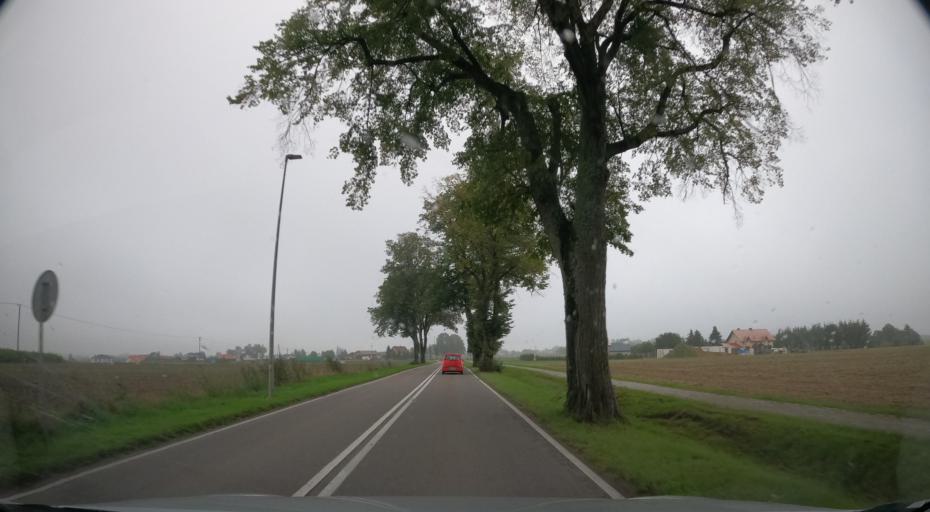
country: PL
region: Pomeranian Voivodeship
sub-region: Powiat wejherowski
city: Bojano
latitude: 54.4527
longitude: 18.3698
